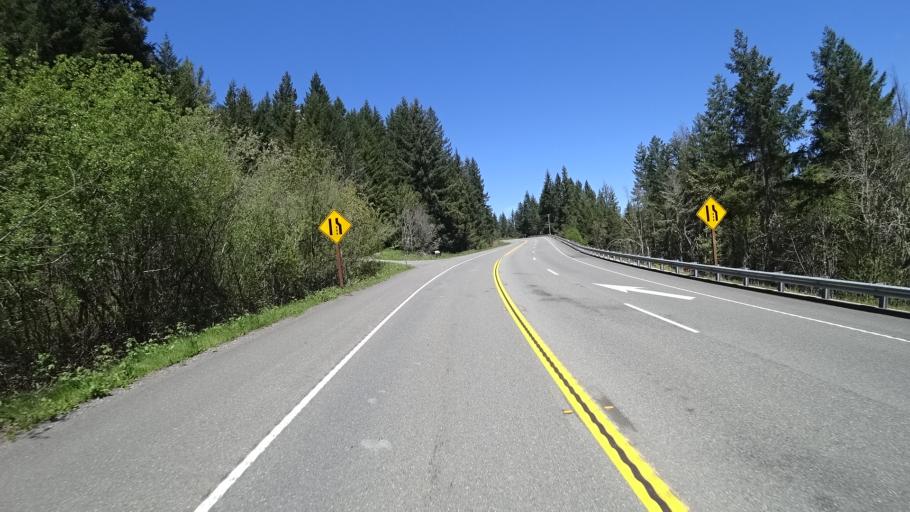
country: US
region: California
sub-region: Humboldt County
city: Blue Lake
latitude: 40.9222
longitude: -123.8368
